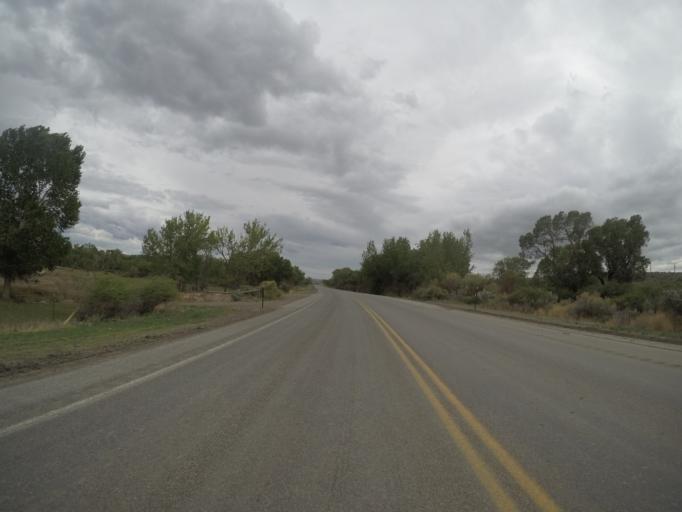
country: US
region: Wyoming
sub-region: Big Horn County
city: Lovell
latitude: 44.8637
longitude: -108.3315
